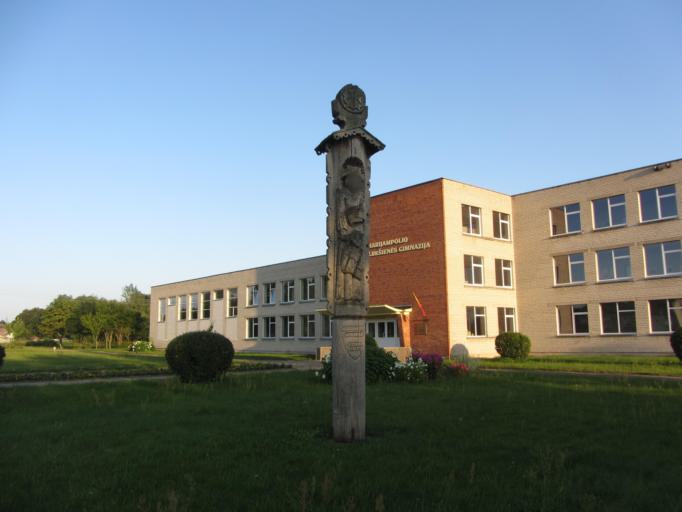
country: LT
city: Skaidiskes
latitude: 54.5327
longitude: 25.3237
